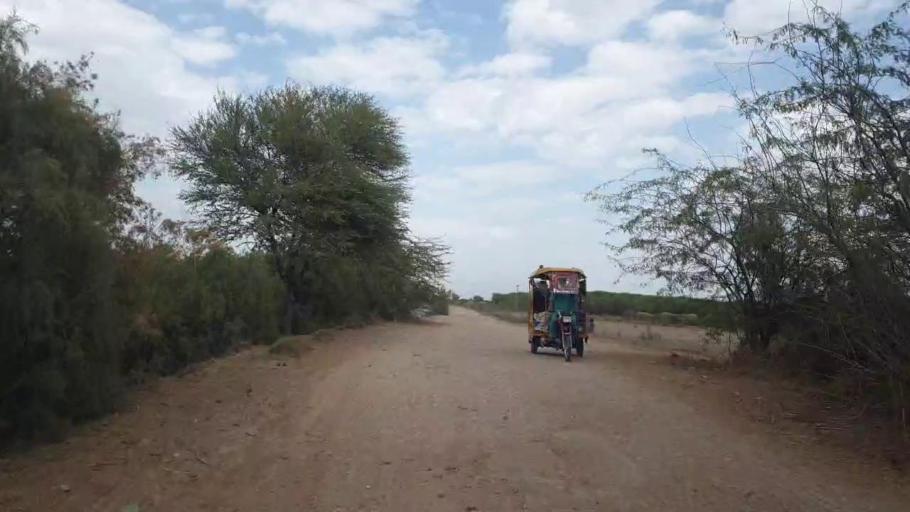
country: PK
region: Sindh
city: Hala
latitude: 25.9551
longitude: 68.4630
